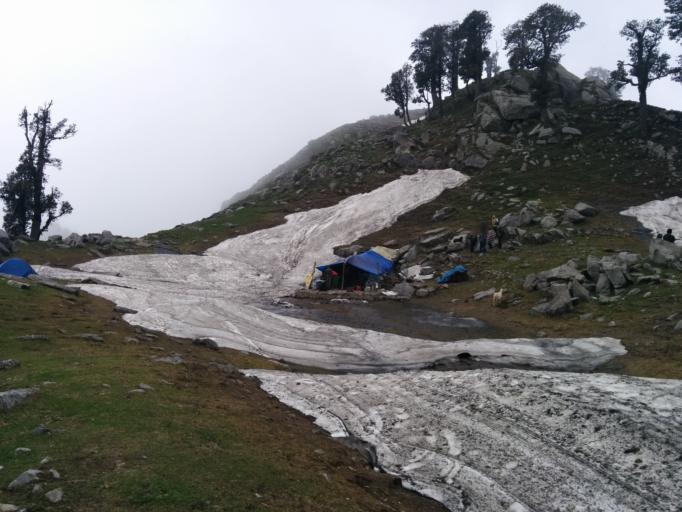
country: IN
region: Himachal Pradesh
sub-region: Kangra
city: Dharmsala
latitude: 32.2744
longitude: 76.3617
